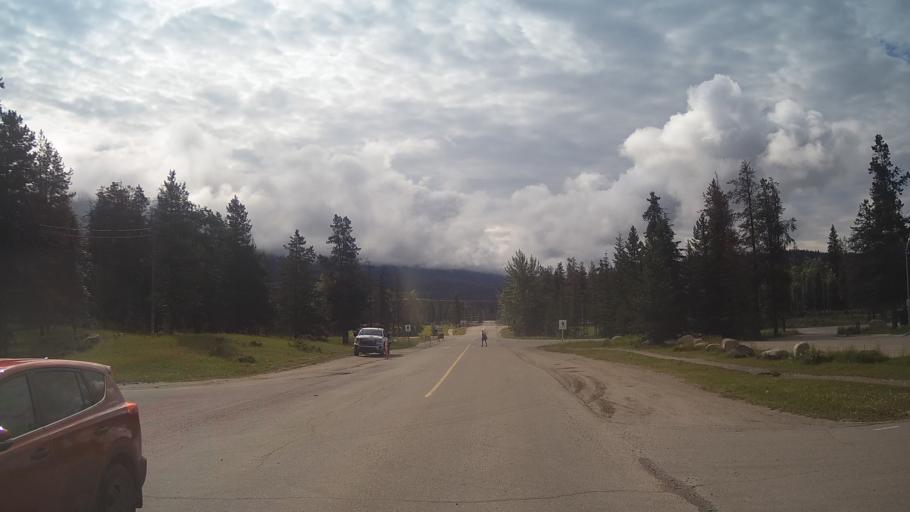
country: CA
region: Alberta
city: Jasper Park Lodge
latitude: 52.8720
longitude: -118.0808
